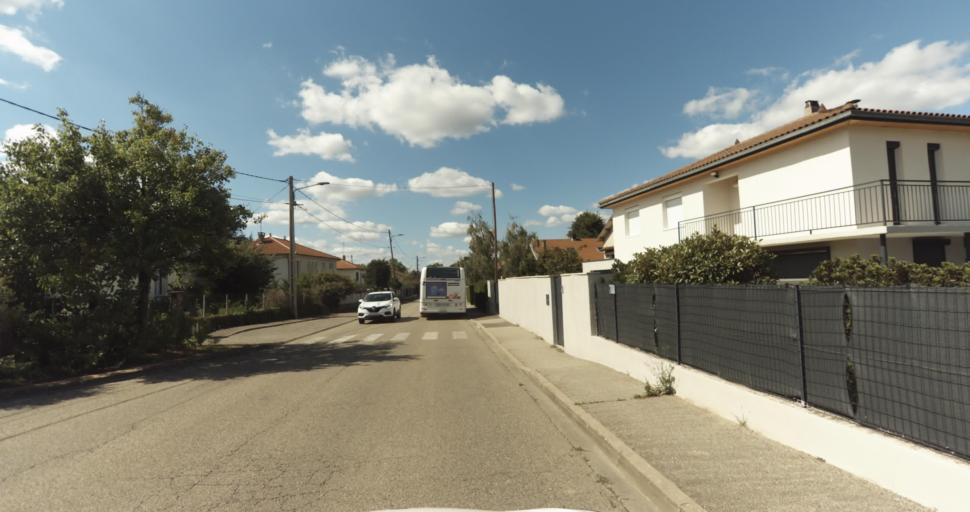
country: FR
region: Rhone-Alpes
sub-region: Departement du Rhone
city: Chaponost
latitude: 45.7047
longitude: 4.7423
